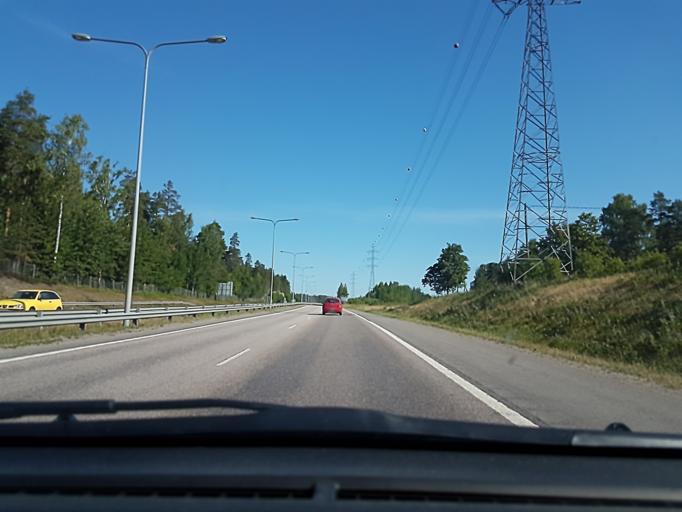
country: FI
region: Uusimaa
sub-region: Helsinki
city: Vantaa
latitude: 60.3120
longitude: 24.9981
